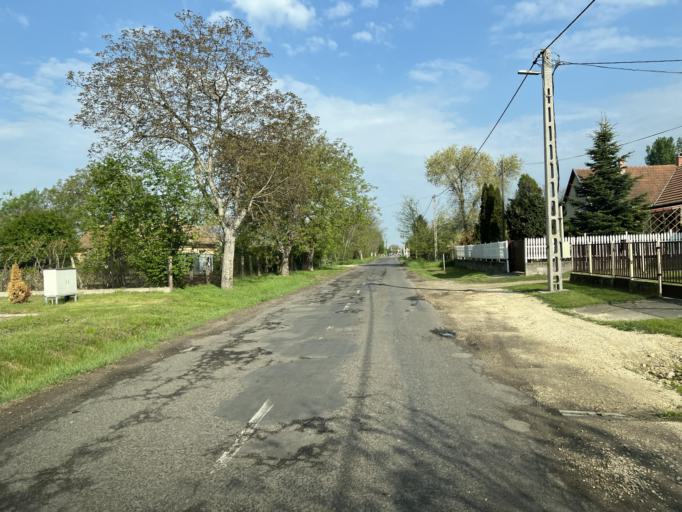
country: HU
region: Pest
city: Abony
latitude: 47.1729
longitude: 20.0262
